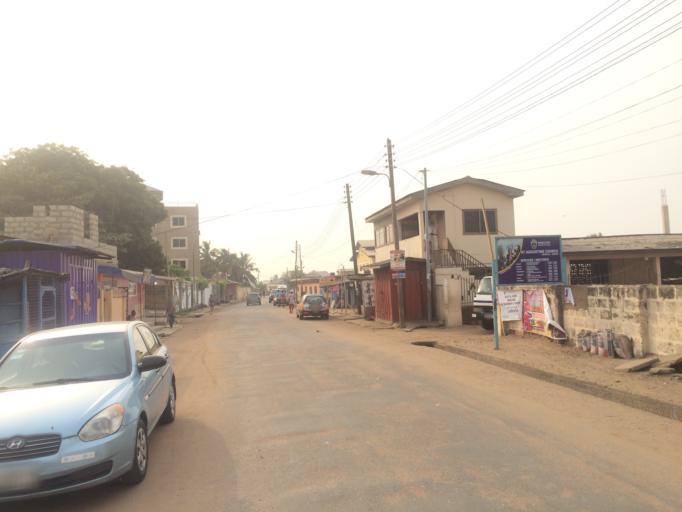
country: GH
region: Greater Accra
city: Nungua
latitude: 5.6029
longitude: -0.0856
